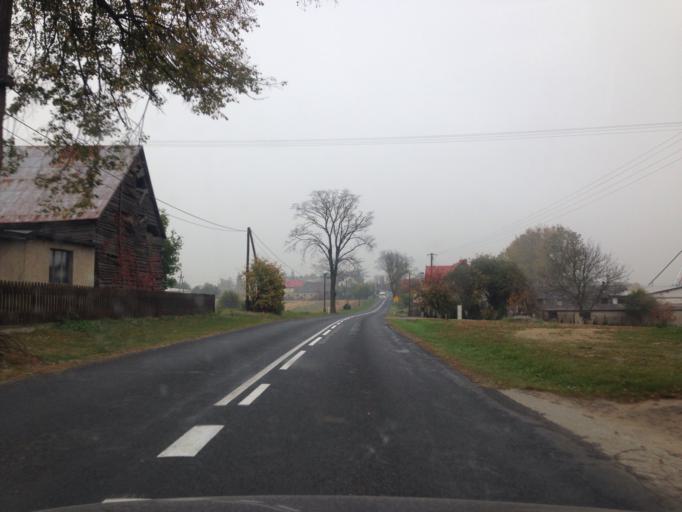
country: PL
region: Kujawsko-Pomorskie
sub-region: Powiat brodnicki
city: Bartniczka
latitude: 53.2497
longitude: 19.5622
